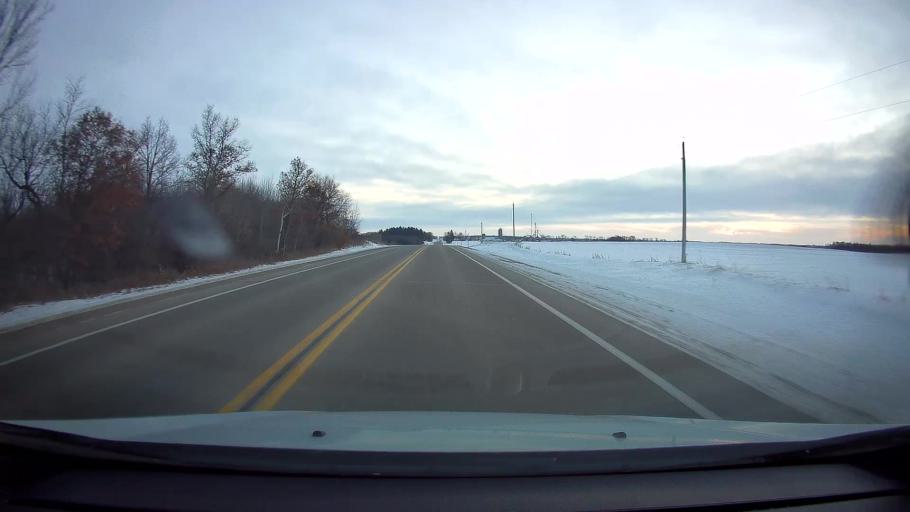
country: US
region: Wisconsin
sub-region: Saint Croix County
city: New Richmond
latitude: 45.1371
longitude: -92.4915
